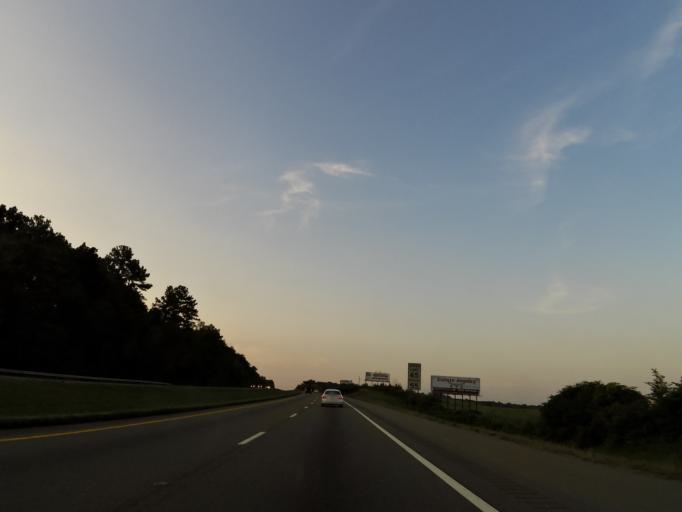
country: US
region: Tennessee
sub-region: Loudon County
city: Lenoir City
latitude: 35.8357
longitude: -84.2736
